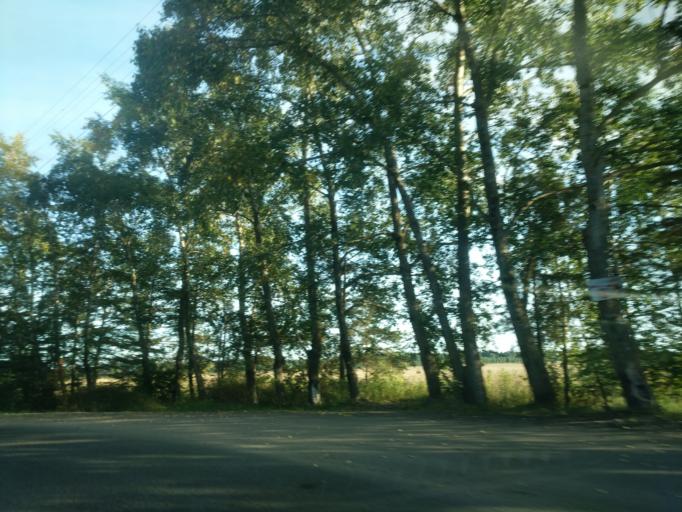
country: RU
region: Kirov
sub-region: Kirovo-Chepetskiy Rayon
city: Kirov
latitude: 58.6148
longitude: 49.7680
